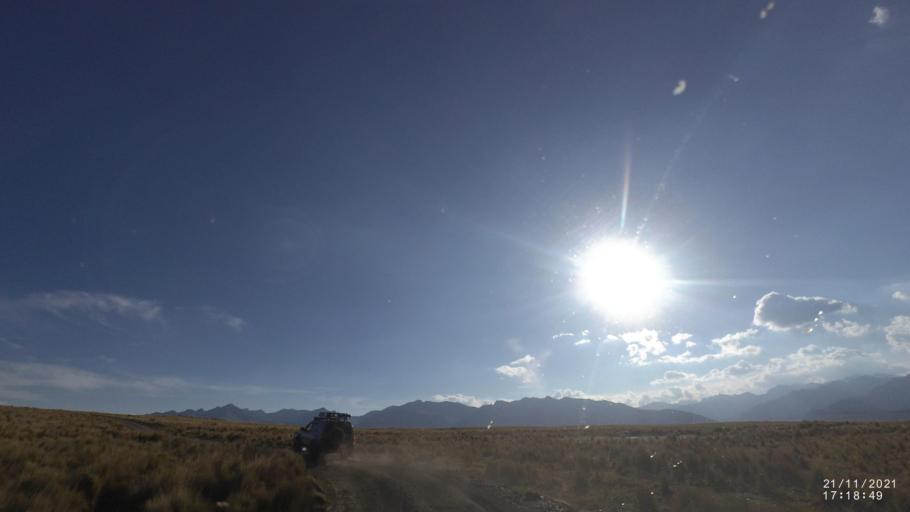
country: BO
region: Cochabamba
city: Cochabamba
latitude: -17.1463
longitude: -66.2582
